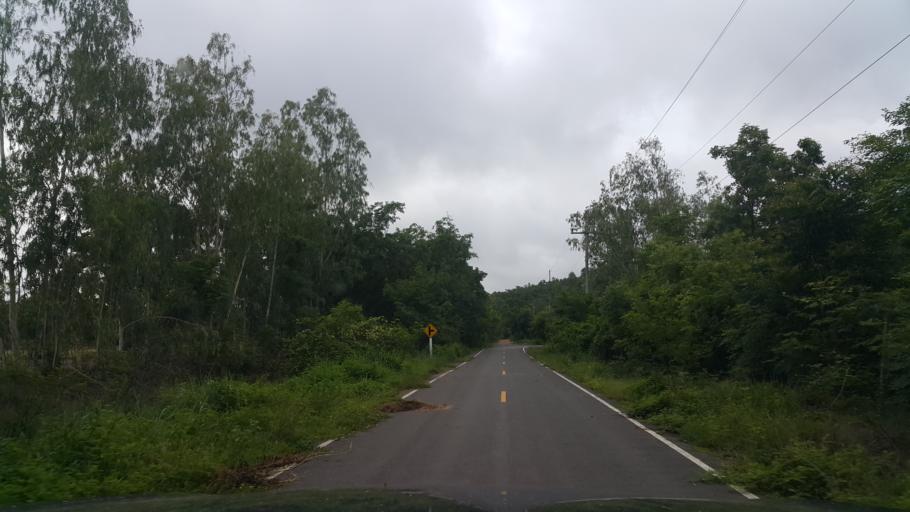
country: TH
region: Sukhothai
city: Sawankhalok
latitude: 17.3065
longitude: 99.7098
